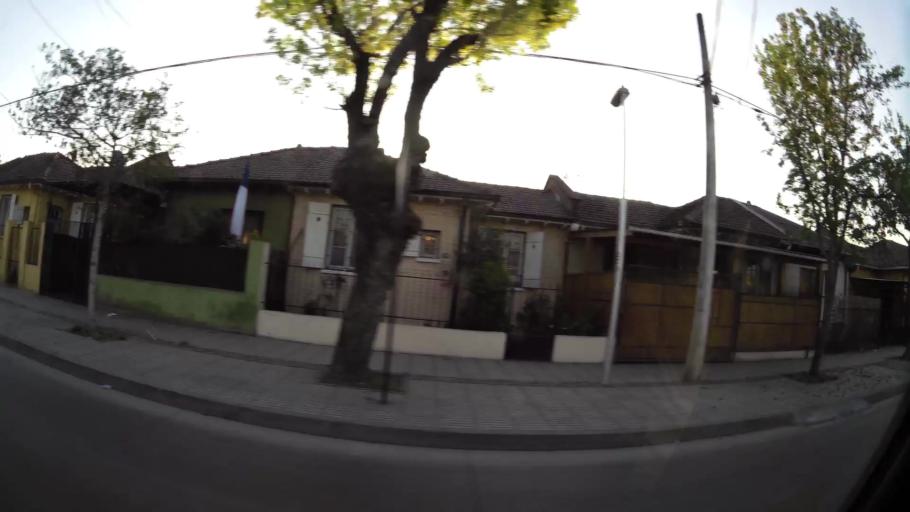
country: CL
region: Santiago Metropolitan
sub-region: Provincia de Santiago
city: Santiago
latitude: -33.4703
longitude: -70.6717
